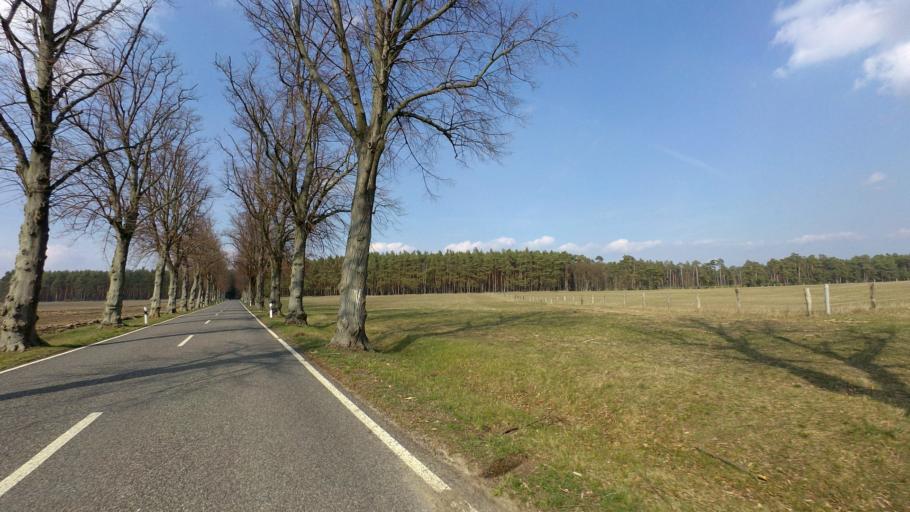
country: DE
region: Brandenburg
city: Dahme
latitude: 51.9434
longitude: 13.4420
